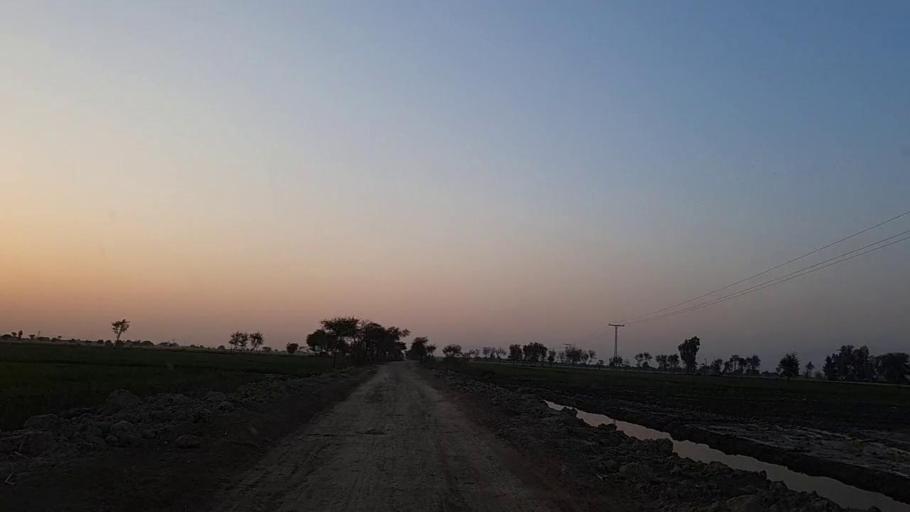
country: PK
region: Sindh
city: Bhit Shah
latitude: 25.9308
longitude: 68.4746
